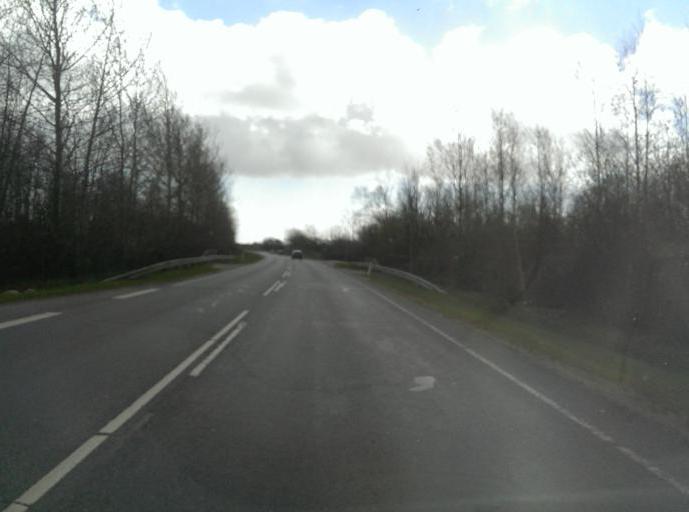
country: DK
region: South Denmark
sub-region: Esbjerg Kommune
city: Esbjerg
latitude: 55.5212
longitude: 8.4074
